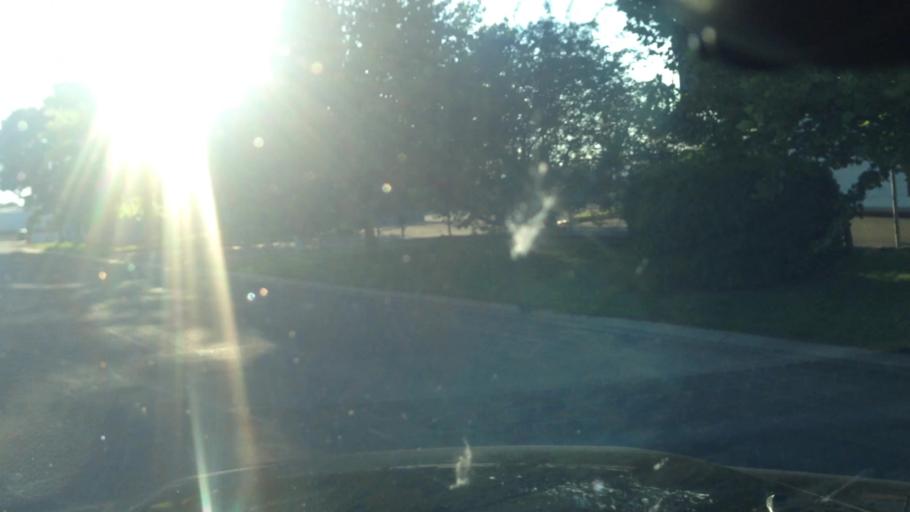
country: US
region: Nevada
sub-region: Washoe County
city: Sparks
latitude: 39.5274
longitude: -119.7201
